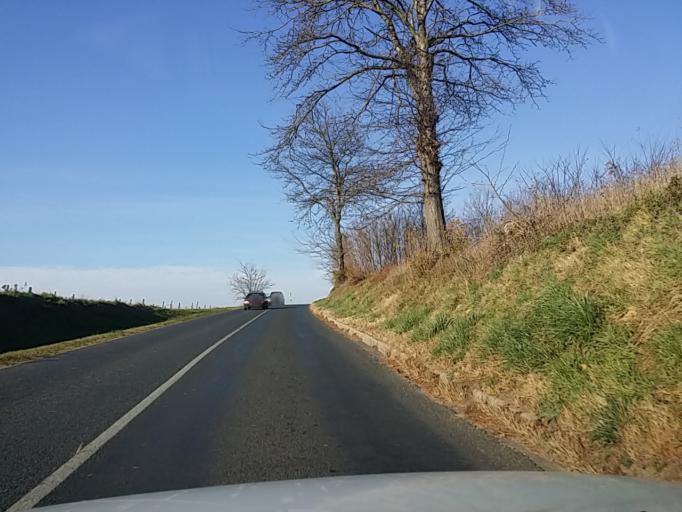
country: HU
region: Veszprem
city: Badacsonytomaj
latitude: 46.8597
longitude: 17.5026
